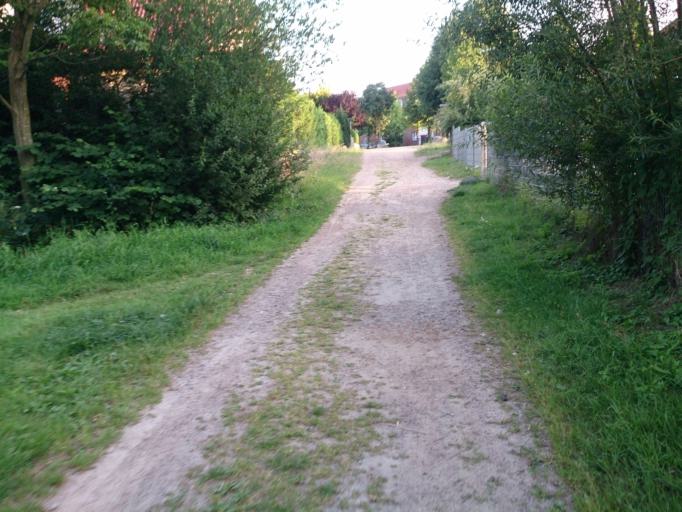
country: DE
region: Hamburg
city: Altona
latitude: 53.4825
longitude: 9.8899
